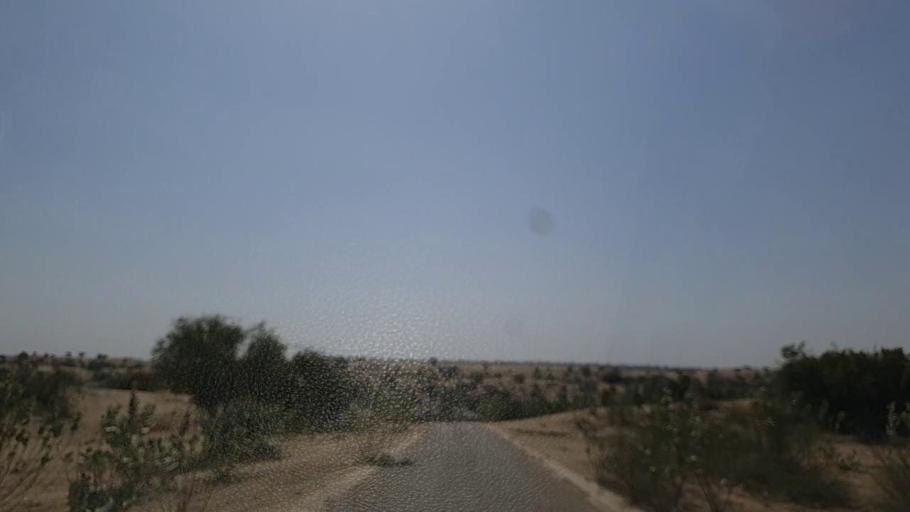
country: PK
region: Sindh
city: Mithi
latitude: 24.7059
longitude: 69.5912
